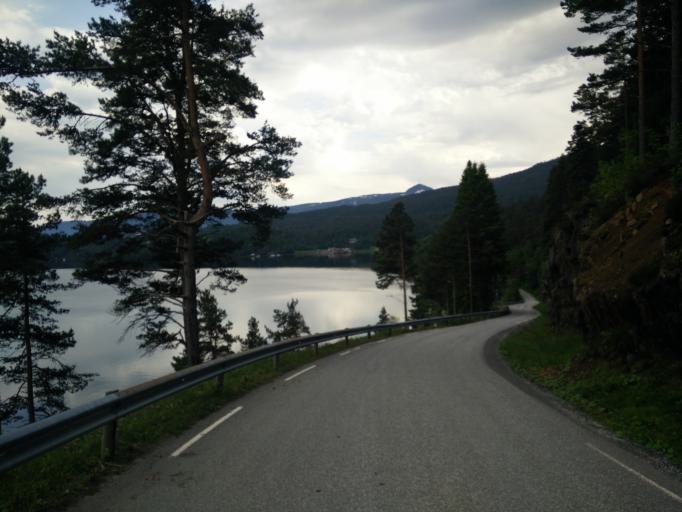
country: NO
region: More og Romsdal
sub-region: Kristiansund
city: Rensvik
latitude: 63.0299
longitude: 7.9548
